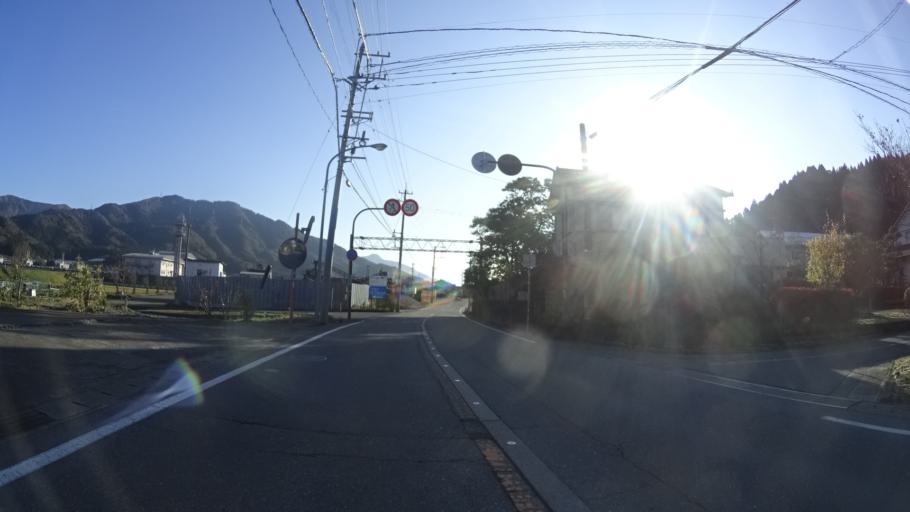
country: JP
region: Fukui
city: Maruoka
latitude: 36.1007
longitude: 136.3181
